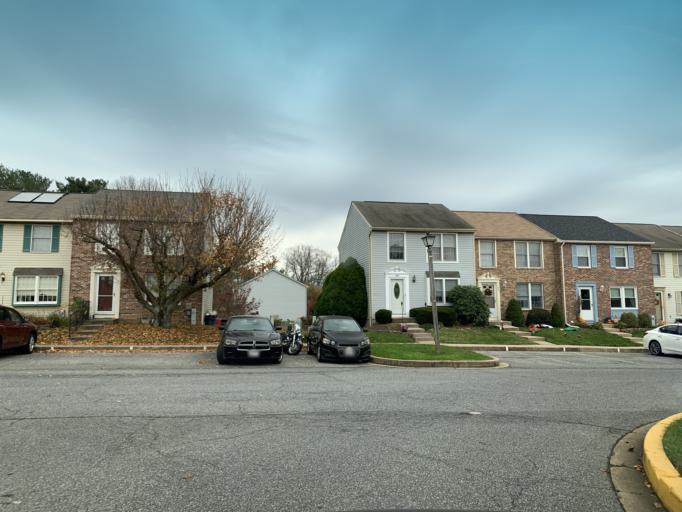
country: US
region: Maryland
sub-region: Harford County
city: Bel Air
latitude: 39.5494
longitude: -76.3437
